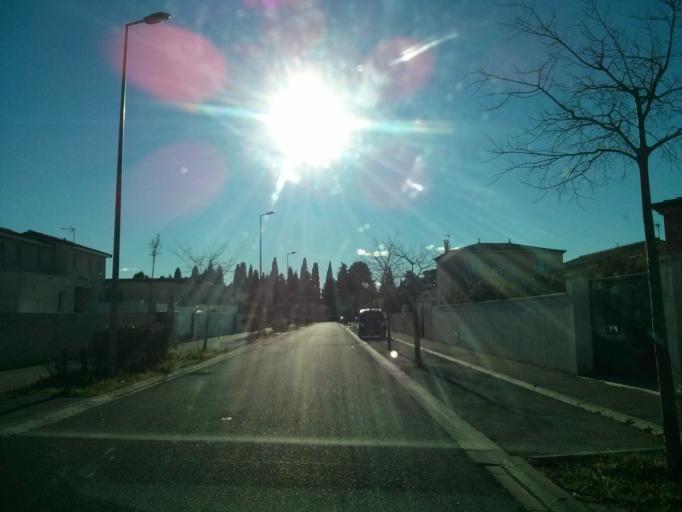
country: FR
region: Languedoc-Roussillon
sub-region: Departement du Gard
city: Calvisson
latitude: 43.7847
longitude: 4.1996
